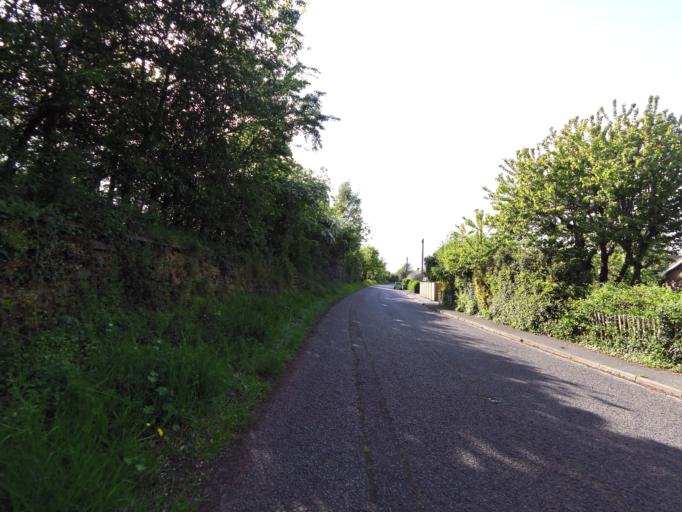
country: GB
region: England
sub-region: Suffolk
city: Beccles
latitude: 52.4469
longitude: 1.6158
